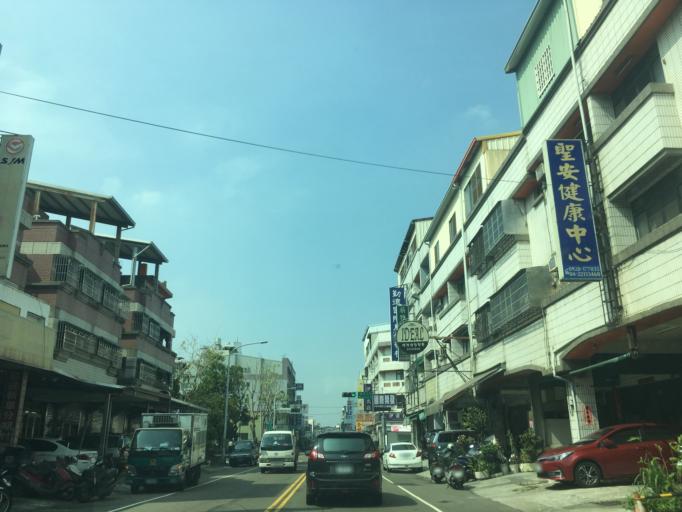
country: TW
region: Taiwan
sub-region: Taichung City
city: Taichung
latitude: 24.1396
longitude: 120.7077
